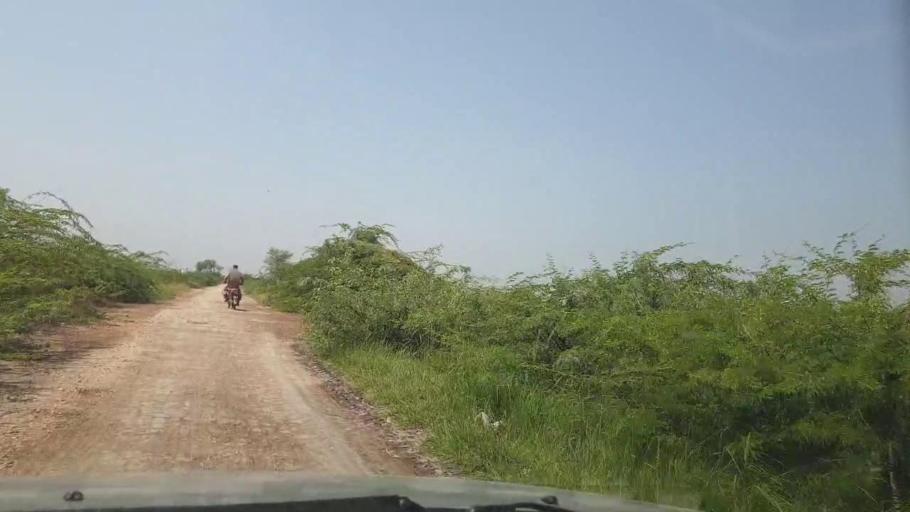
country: PK
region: Sindh
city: Tando Ghulam Ali
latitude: 25.1141
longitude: 68.7934
